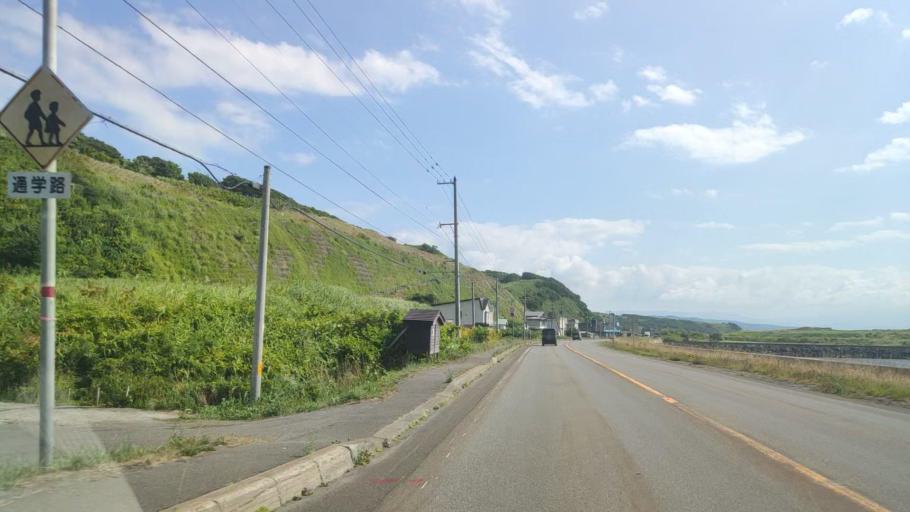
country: JP
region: Hokkaido
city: Rumoi
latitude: 43.9784
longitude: 141.6464
